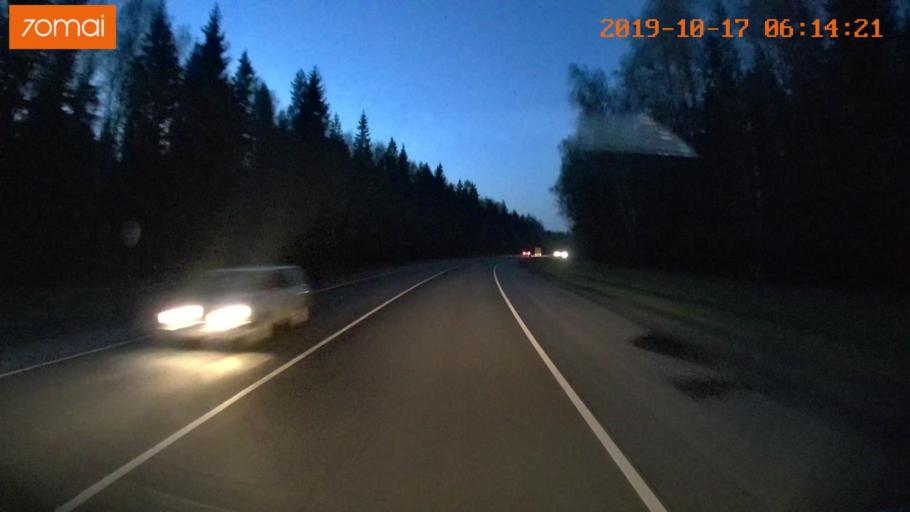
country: RU
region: Ivanovo
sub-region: Gorod Ivanovo
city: Ivanovo
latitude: 56.8869
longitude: 40.9430
